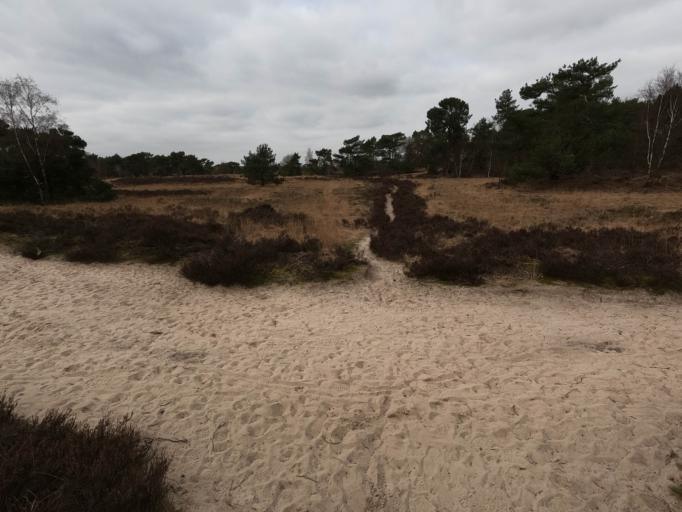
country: BE
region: Flanders
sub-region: Provincie Antwerpen
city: Kalmthout
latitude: 51.3813
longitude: 4.4470
